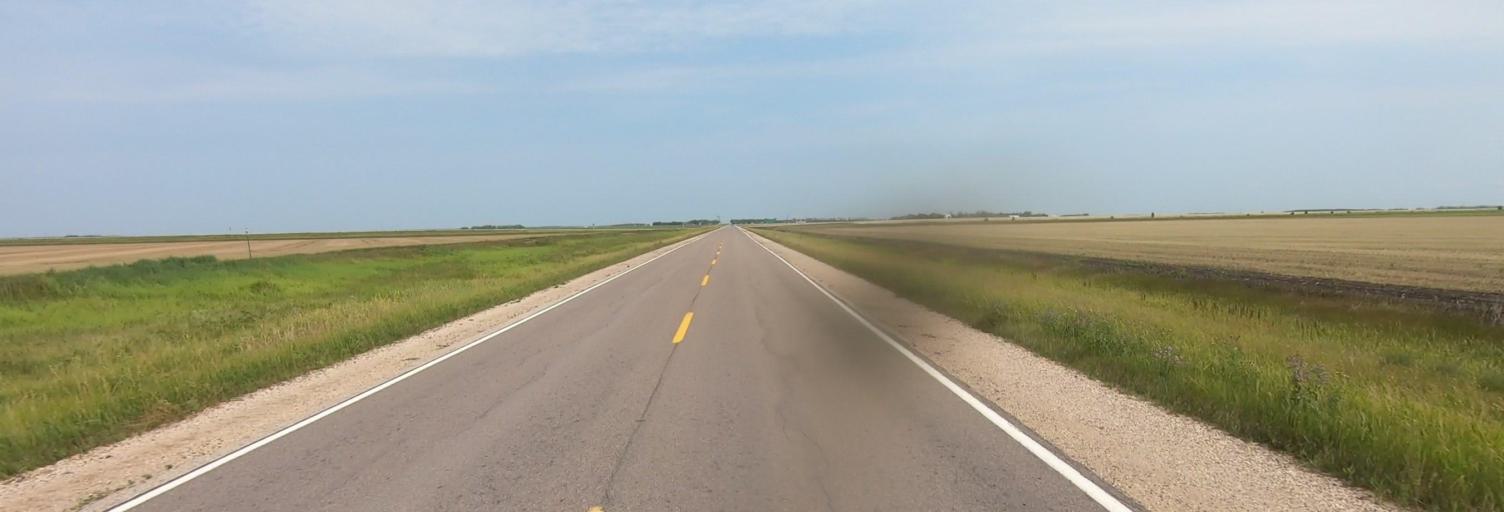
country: CA
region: Manitoba
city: Morris
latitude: 49.5874
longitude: -97.3405
